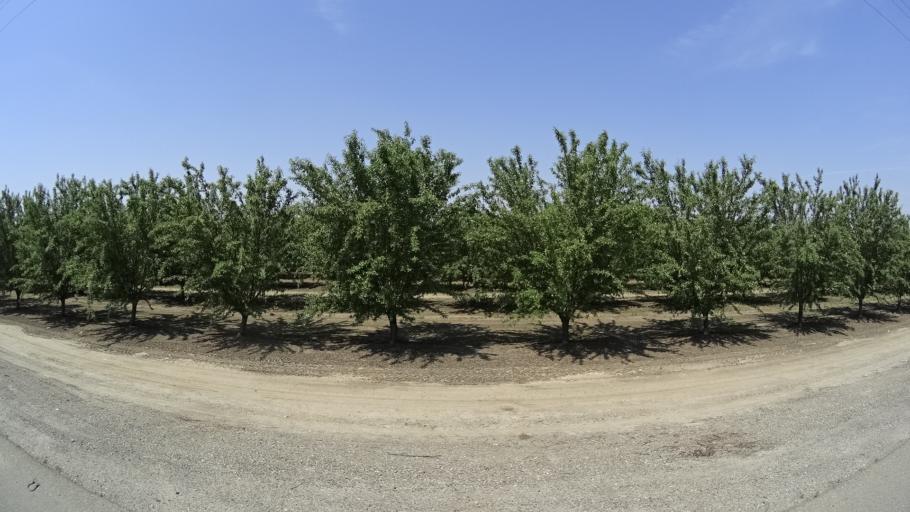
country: US
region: California
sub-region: Kings County
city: Lemoore
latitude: 36.3214
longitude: -119.7808
